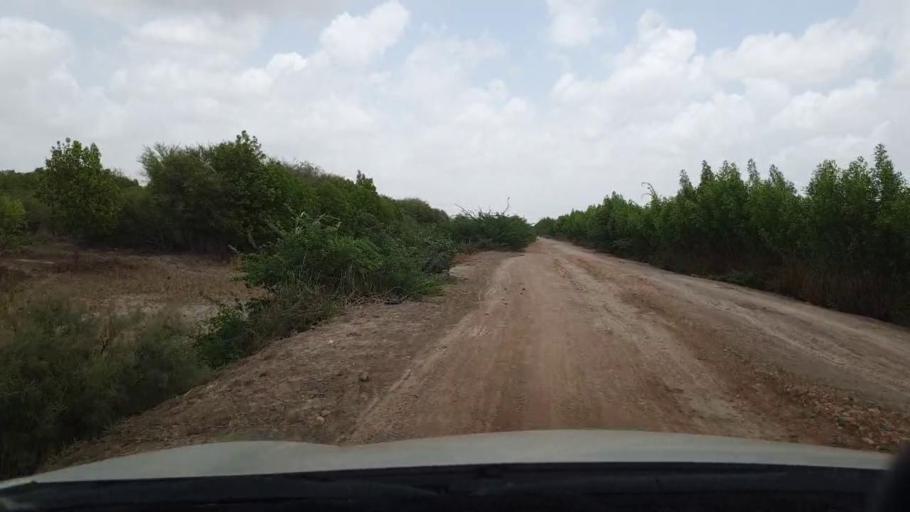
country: PK
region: Sindh
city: Kadhan
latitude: 24.3603
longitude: 68.9575
